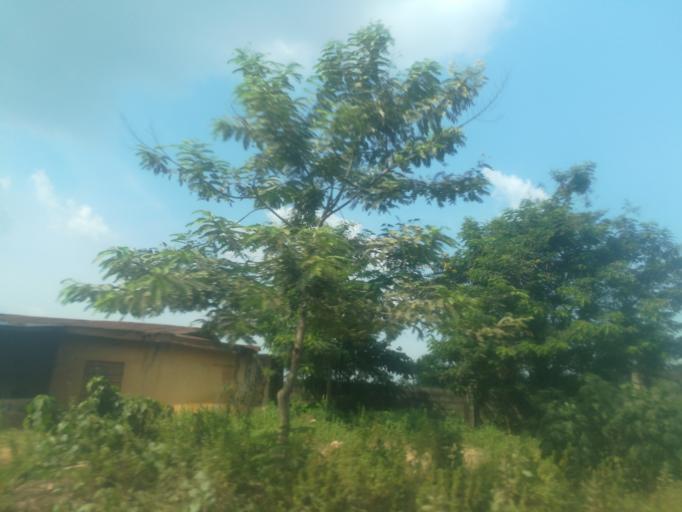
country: NG
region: Ogun
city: Abeokuta
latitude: 7.1718
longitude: 3.3691
